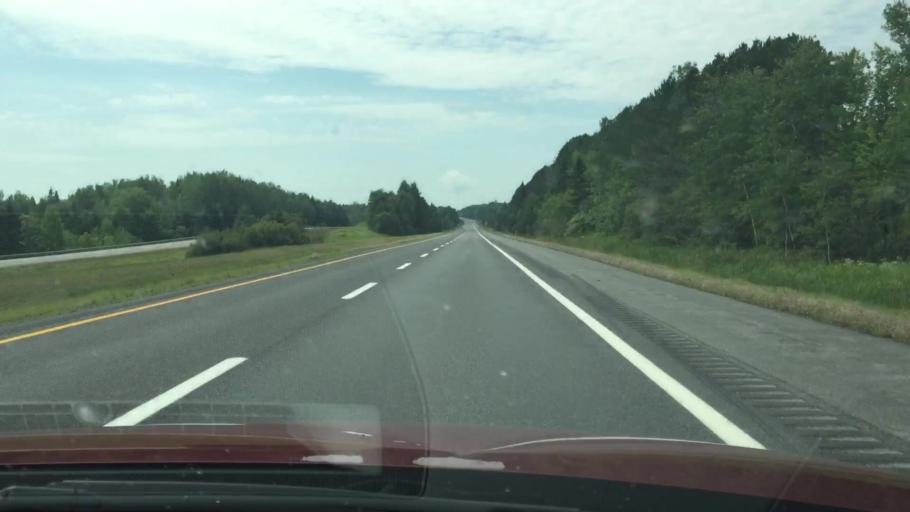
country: US
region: Maine
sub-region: Aroostook County
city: Hodgdon
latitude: 46.1415
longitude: -68.0692
